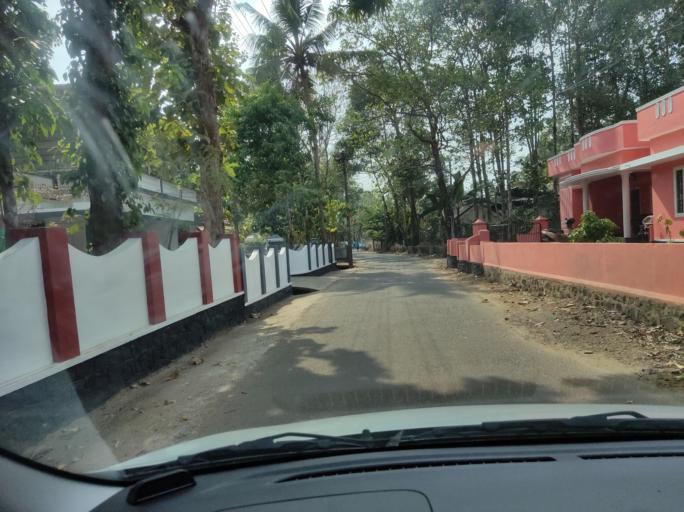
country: IN
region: Kerala
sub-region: Kottayam
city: Kottayam
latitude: 9.6854
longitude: 76.5043
